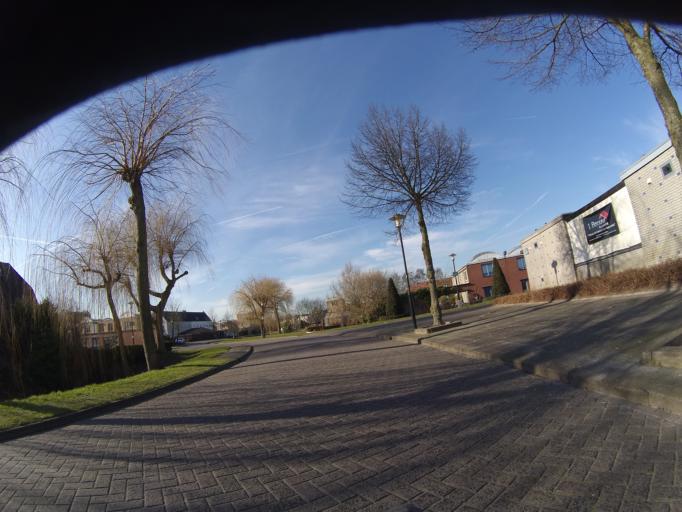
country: NL
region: Utrecht
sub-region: Gemeente Amersfoort
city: Hoogland
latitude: 52.1926
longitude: 5.3980
